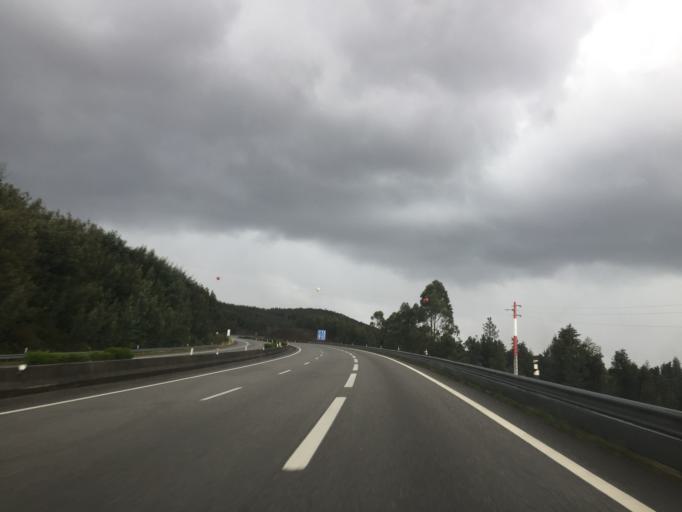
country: PT
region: Aveiro
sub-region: Agueda
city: Valongo
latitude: 40.6621
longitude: -8.3928
